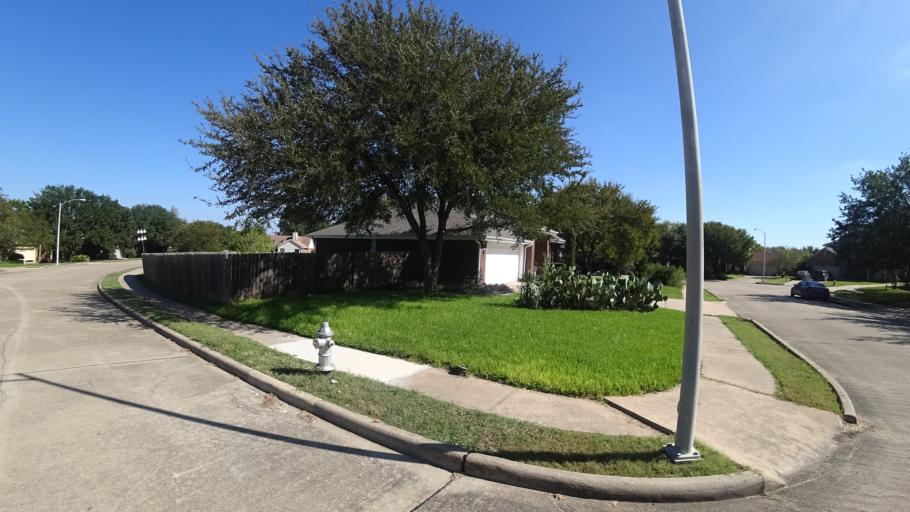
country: US
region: Texas
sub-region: Travis County
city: Manor
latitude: 30.3510
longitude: -97.6143
